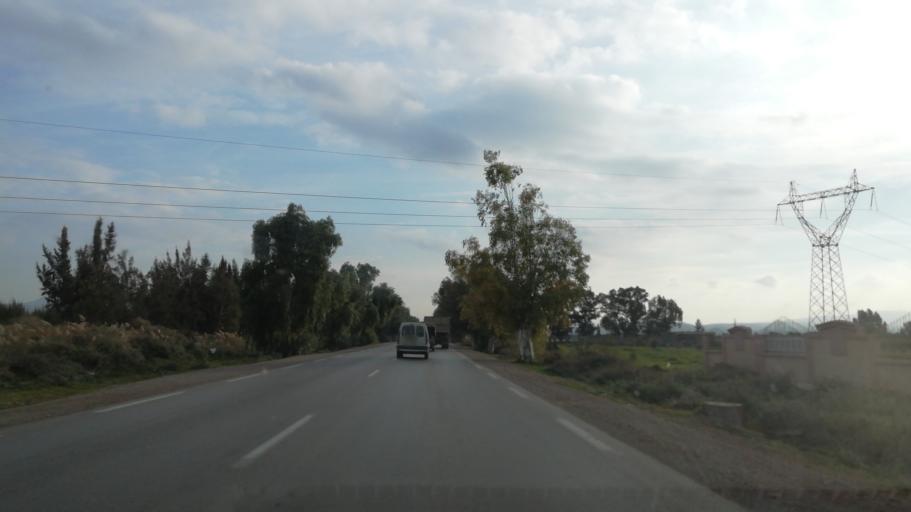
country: DZ
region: Mascara
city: Mascara
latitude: 35.6375
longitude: 0.0606
